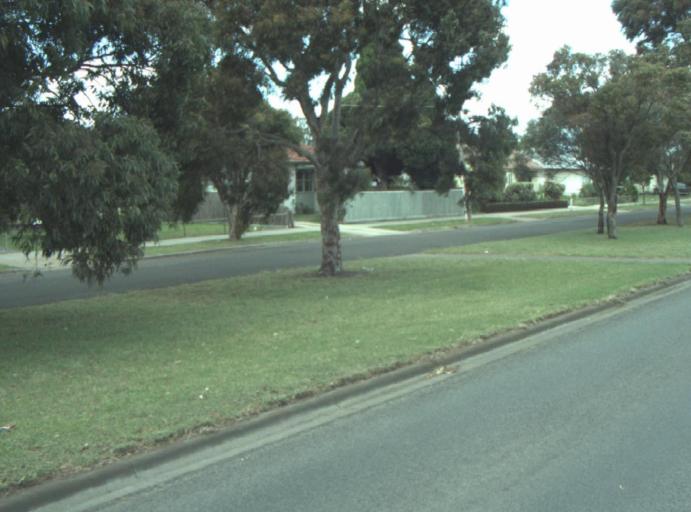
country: AU
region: Victoria
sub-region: Greater Geelong
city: Bell Park
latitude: -38.0766
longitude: 144.3586
